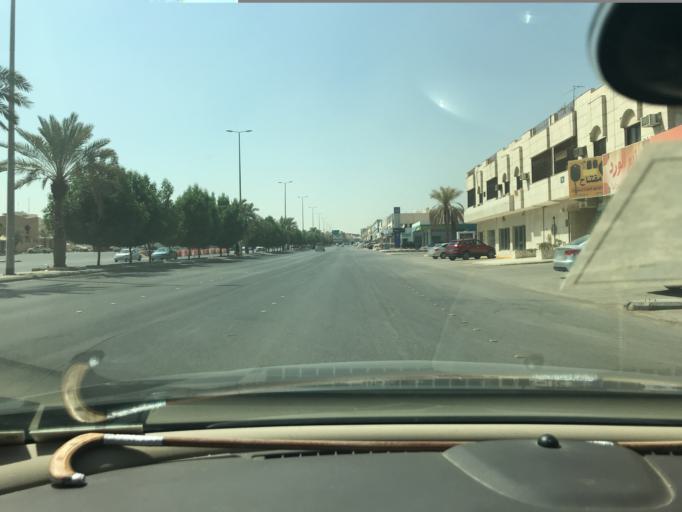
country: SA
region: Ar Riyad
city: Riyadh
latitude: 24.7053
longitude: 46.7829
